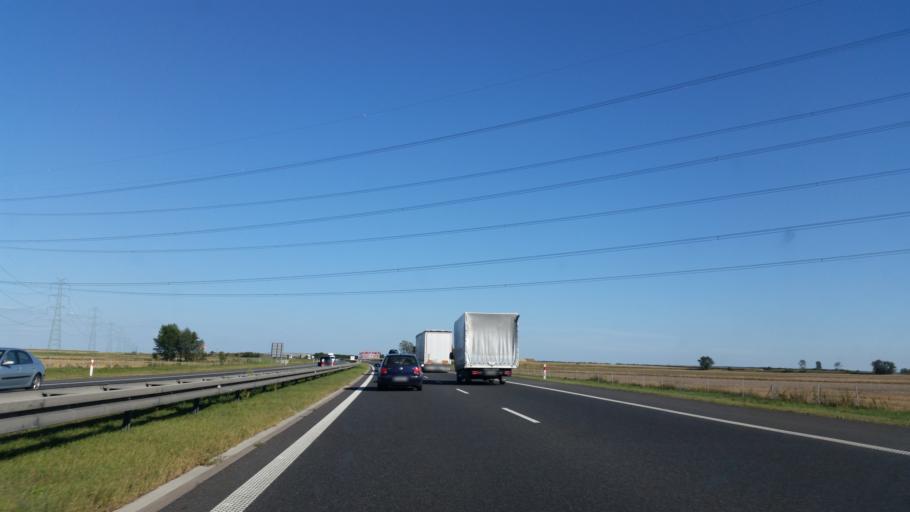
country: PL
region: Opole Voivodeship
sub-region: Powiat brzeski
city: Olszanka
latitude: 50.7420
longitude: 17.4585
